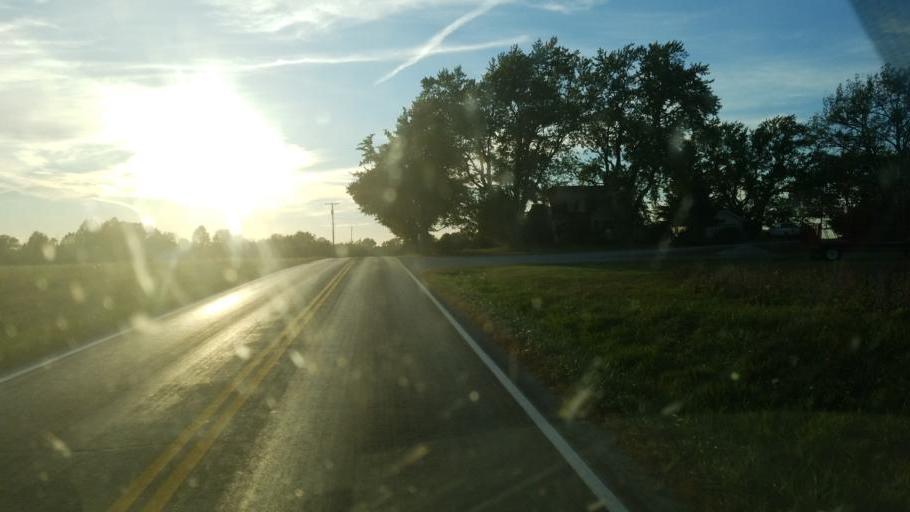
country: US
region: Ohio
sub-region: Ashland County
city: Ashland
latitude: 40.8660
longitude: -82.3911
